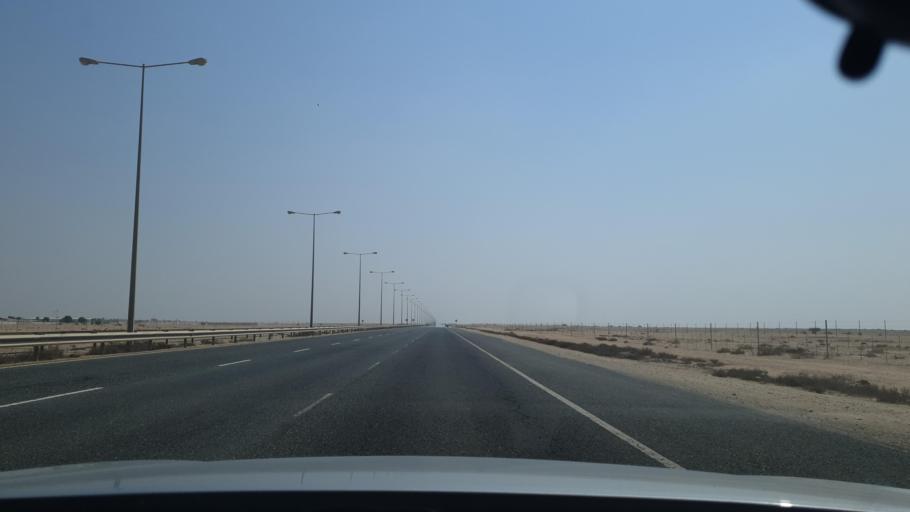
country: QA
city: Al Ghuwayriyah
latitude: 25.8127
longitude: 51.3725
